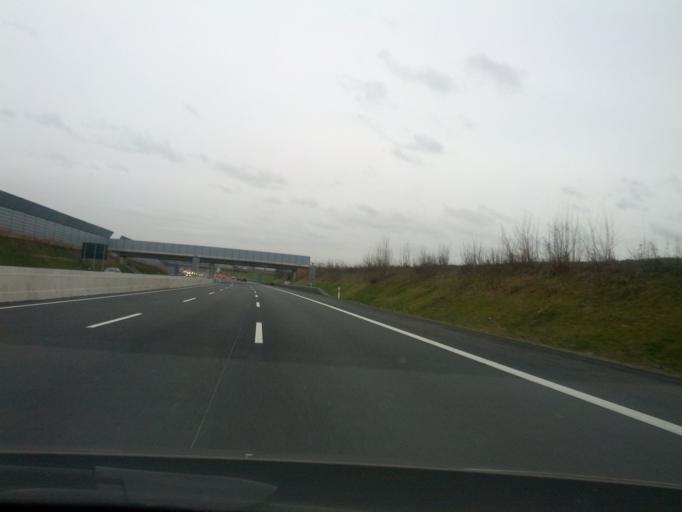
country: DE
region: Lower Saxony
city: Bockenem
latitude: 52.0063
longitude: 10.1590
